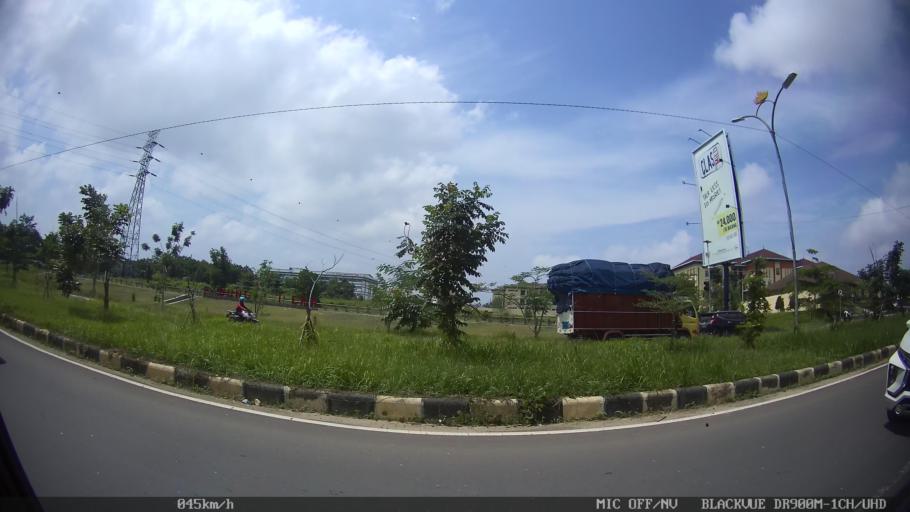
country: ID
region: Lampung
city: Kedaton
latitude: -5.3582
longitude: 105.3081
